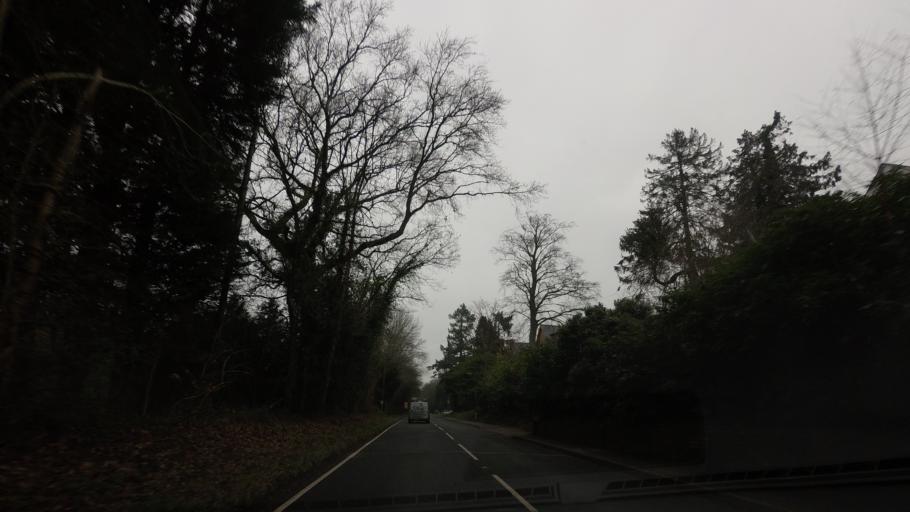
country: GB
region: England
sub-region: Kent
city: Hawkhurst
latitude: 51.0573
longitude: 0.5061
